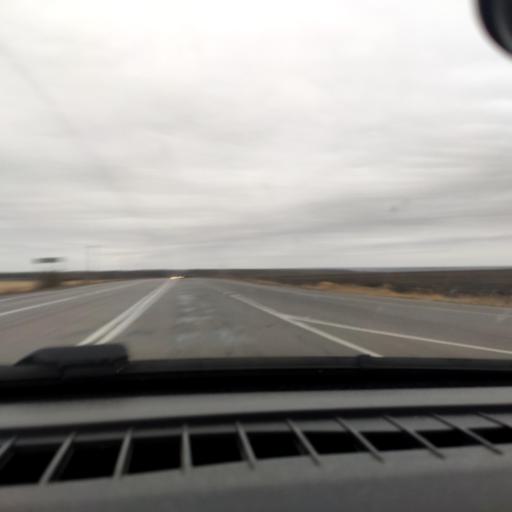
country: RU
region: Voronezj
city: Strelitsa
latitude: 51.5317
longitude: 38.9694
